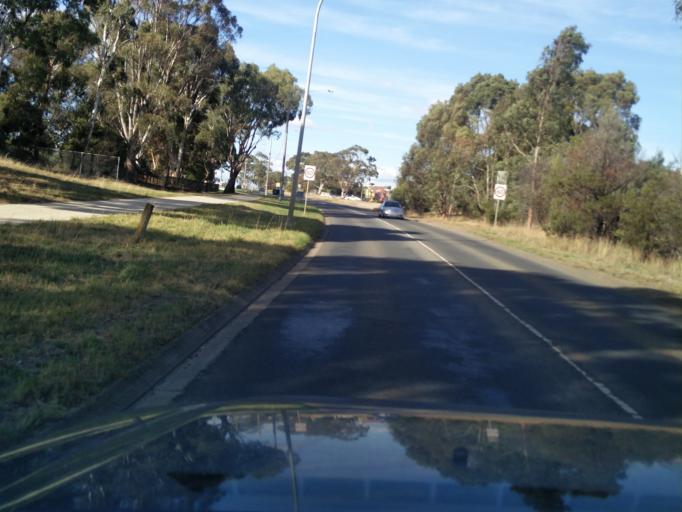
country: AU
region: Victoria
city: Macleod
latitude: -37.7286
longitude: 145.0551
